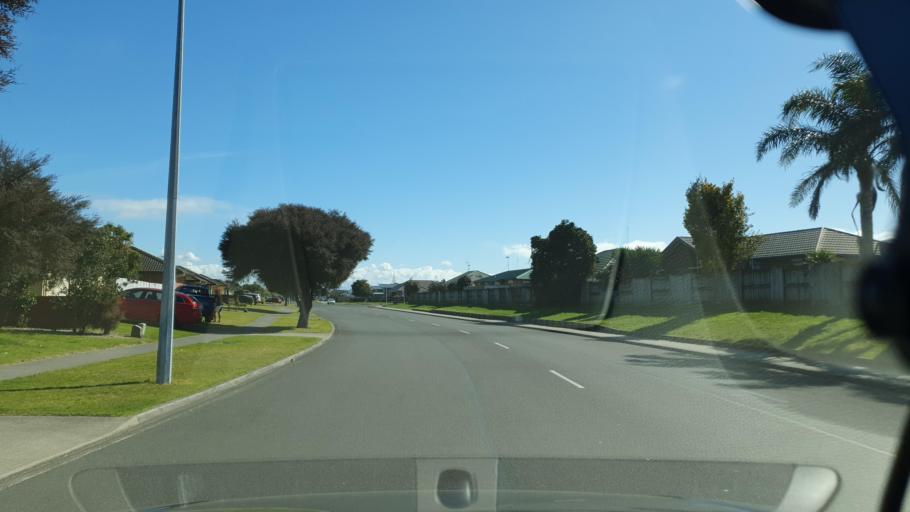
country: NZ
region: Bay of Plenty
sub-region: Tauranga City
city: Tauranga
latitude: -37.7079
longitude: 176.2930
